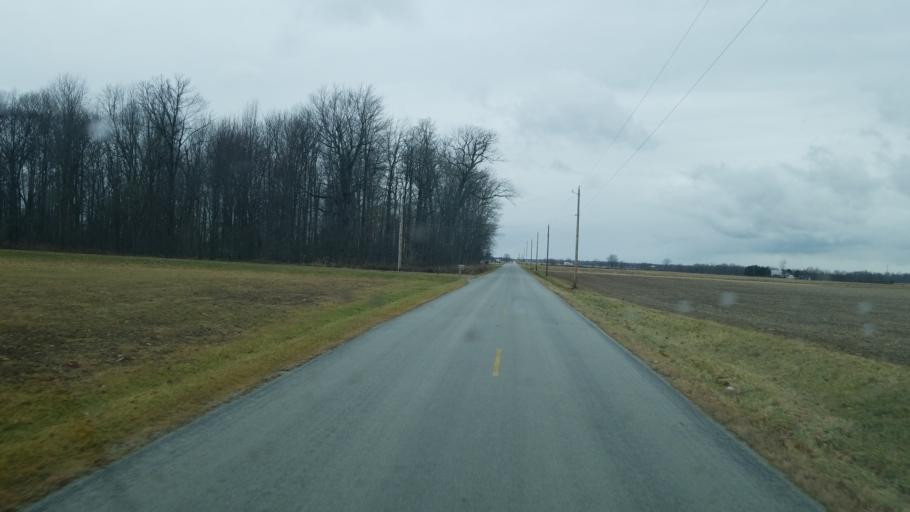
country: US
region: Ohio
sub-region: Hardin County
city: Kenton
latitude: 40.7024
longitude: -83.5637
